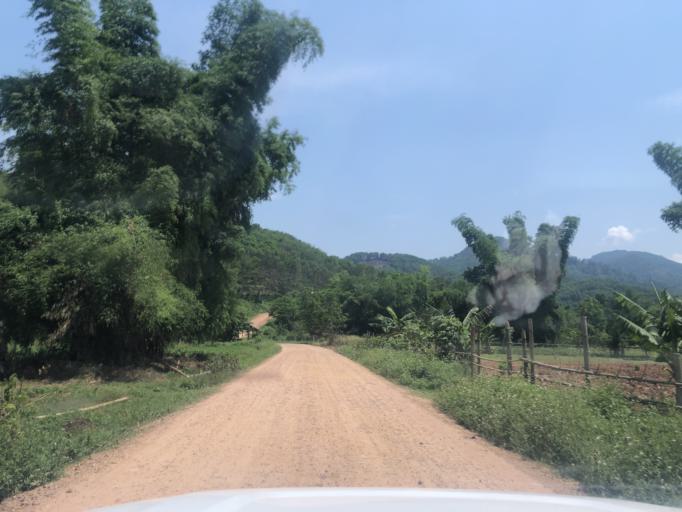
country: LA
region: Phongsali
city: Phongsali
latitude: 21.4120
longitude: 101.9693
